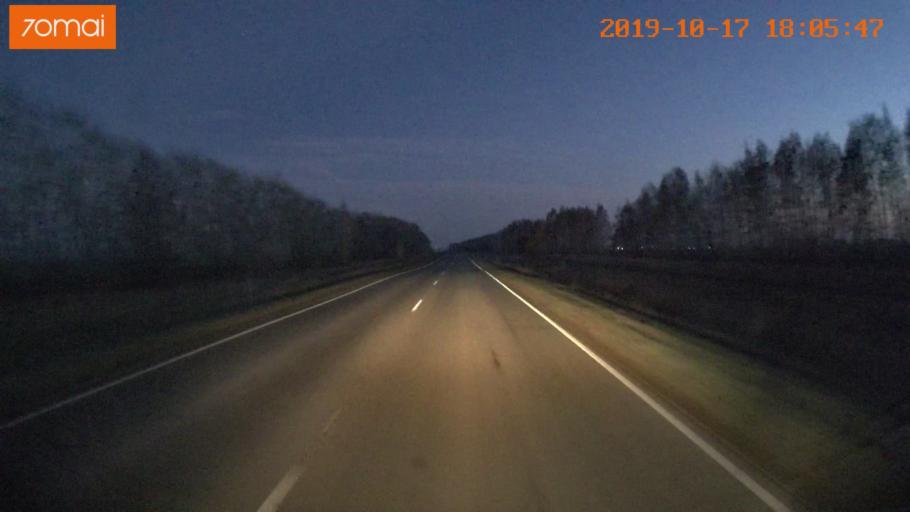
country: RU
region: Tula
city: Kurkino
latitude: 53.4612
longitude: 38.6480
